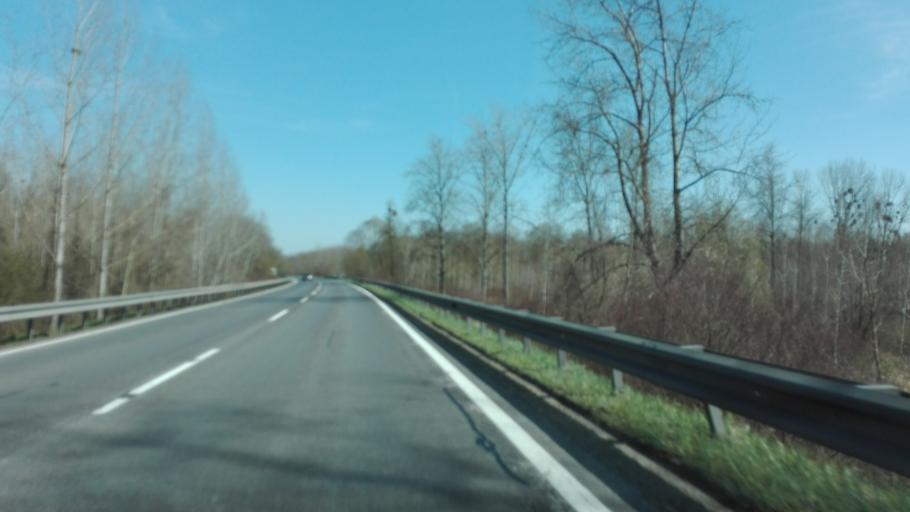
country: AT
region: Upper Austria
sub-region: Politischer Bezirk Linz-Land
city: Enns
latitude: 48.2481
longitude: 14.4546
